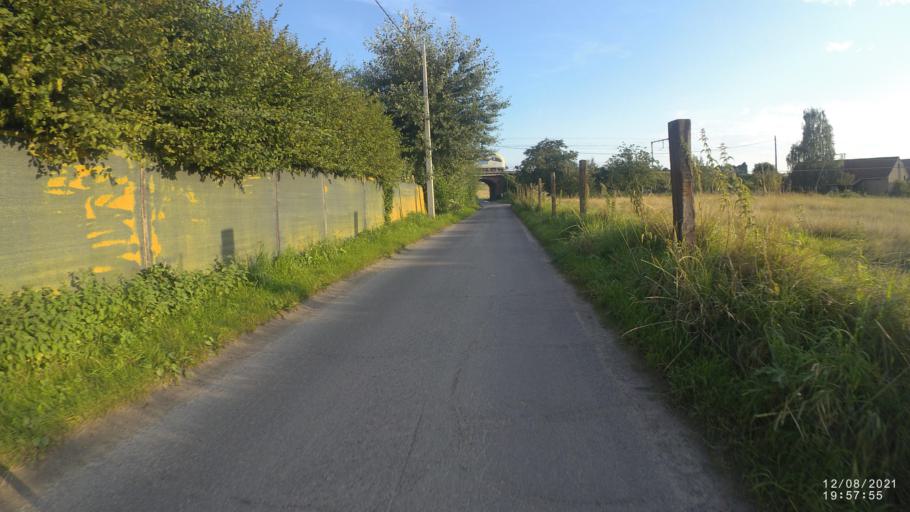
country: BE
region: Flanders
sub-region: Provincie Vlaams-Brabant
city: Dilbeek
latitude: 50.8694
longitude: 4.2274
